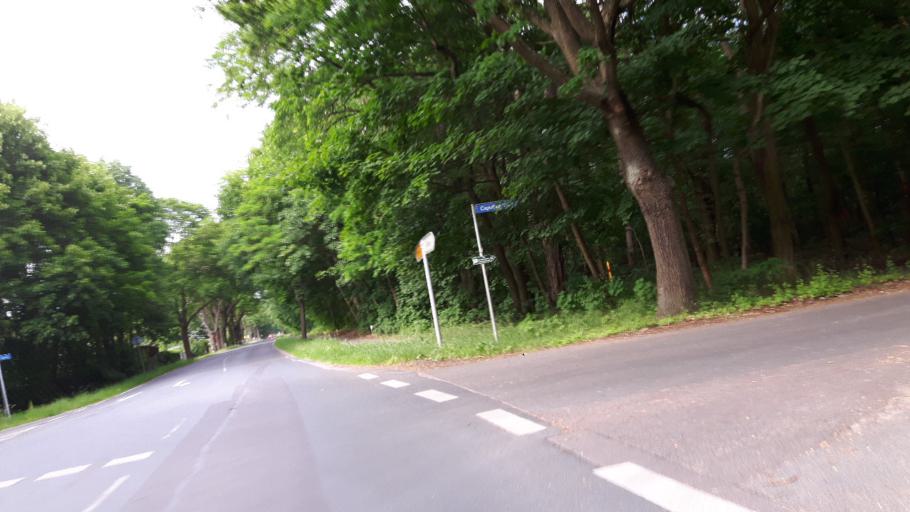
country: DE
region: Brandenburg
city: Michendorf
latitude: 52.3213
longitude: 13.0346
